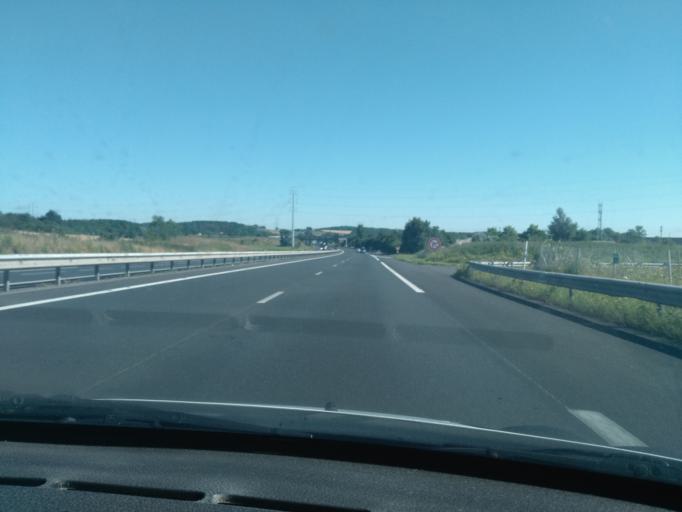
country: FR
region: Rhone-Alpes
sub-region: Departement du Rhone
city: Cailloux-sur-Fontaines
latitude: 45.8559
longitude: 4.9091
